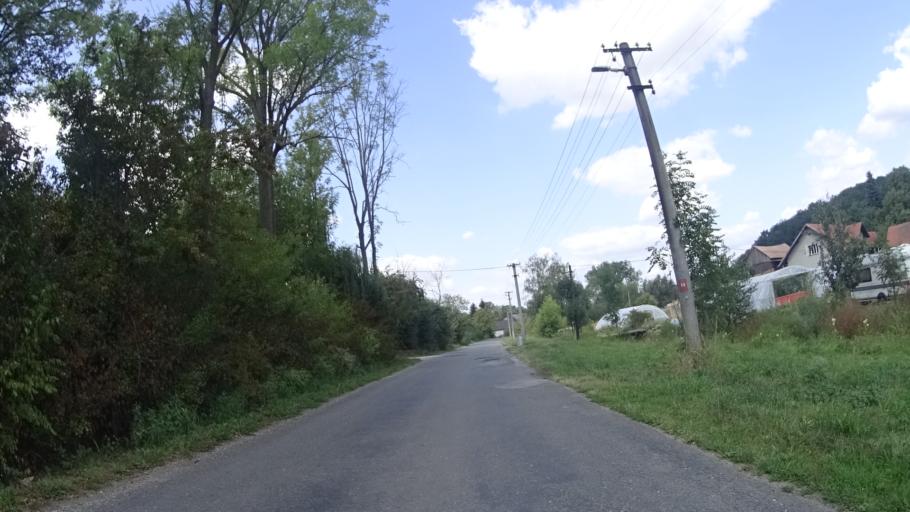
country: CZ
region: Kralovehradecky
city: Kopidlno
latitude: 50.3837
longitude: 15.2999
